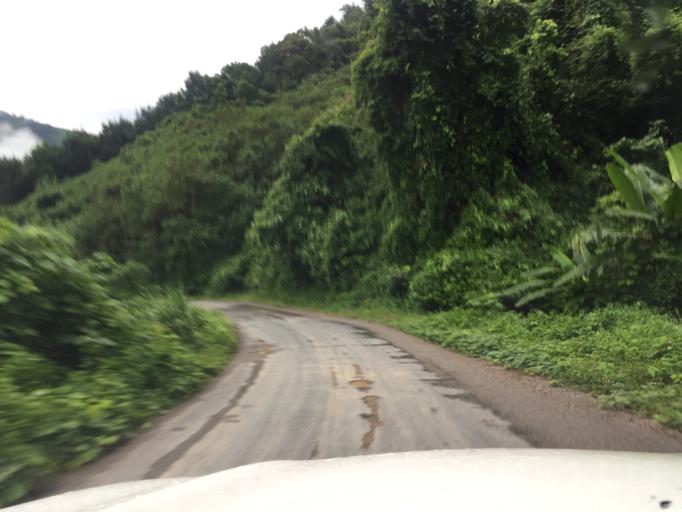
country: LA
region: Oudomxai
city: Muang La
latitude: 21.0152
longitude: 102.2317
